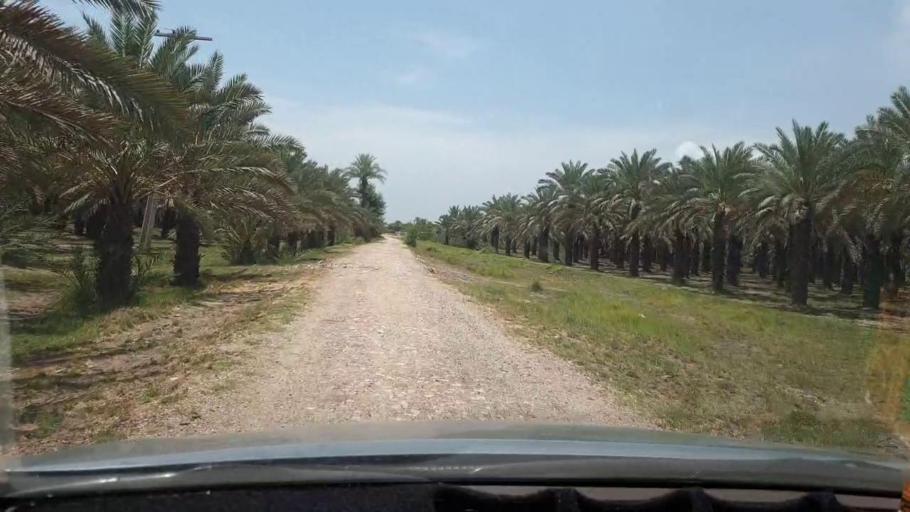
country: PK
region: Sindh
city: Khairpur
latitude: 27.4556
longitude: 68.7805
